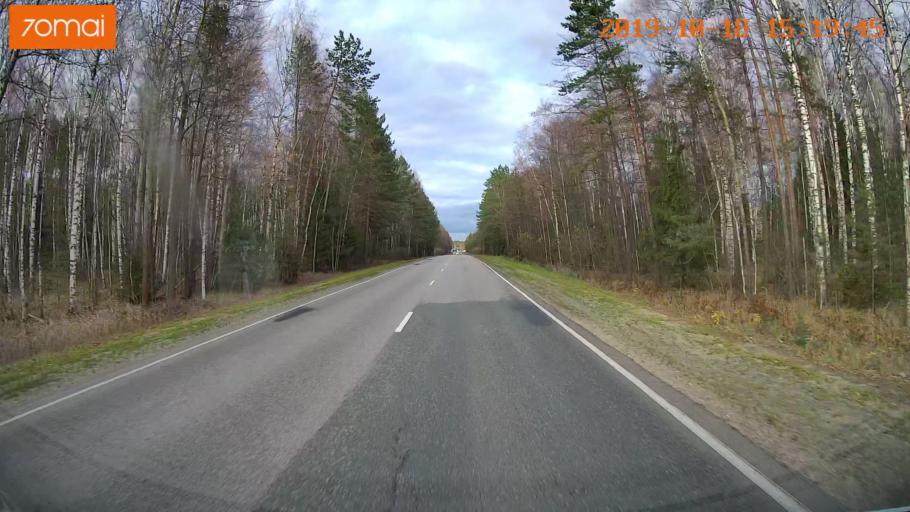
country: RU
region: Vladimir
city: Anopino
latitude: 55.6777
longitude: 40.7401
